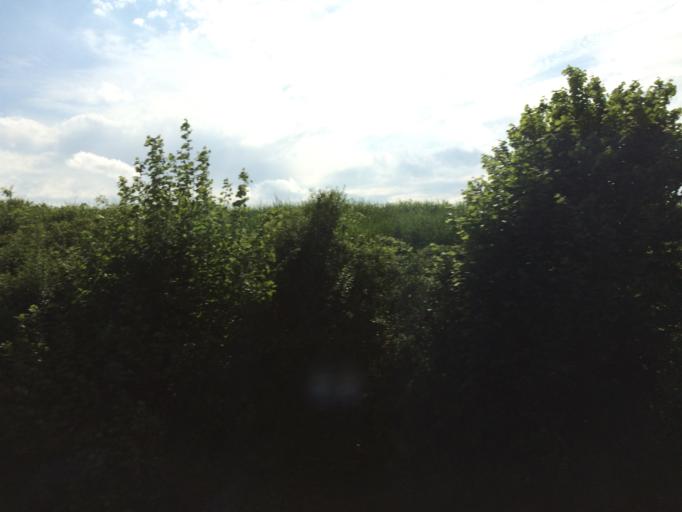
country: DE
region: Bavaria
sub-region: Regierungsbezirk Unterfranken
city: Biebelried
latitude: 49.7941
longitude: 10.0835
